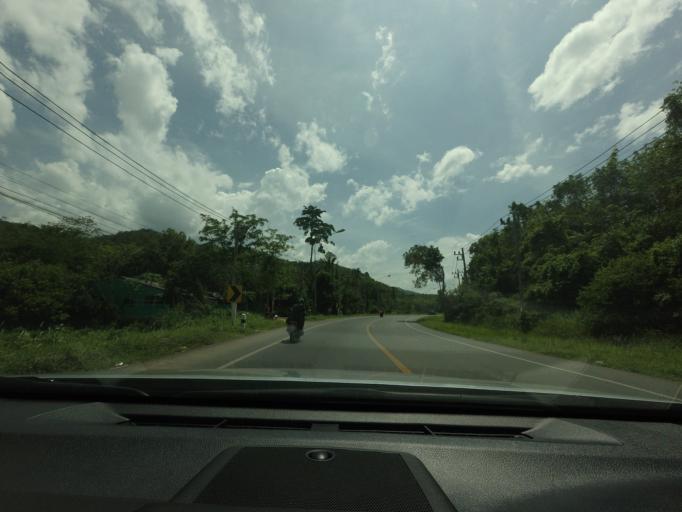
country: TH
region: Yala
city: Krong Pi Nang
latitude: 6.4590
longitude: 101.3324
